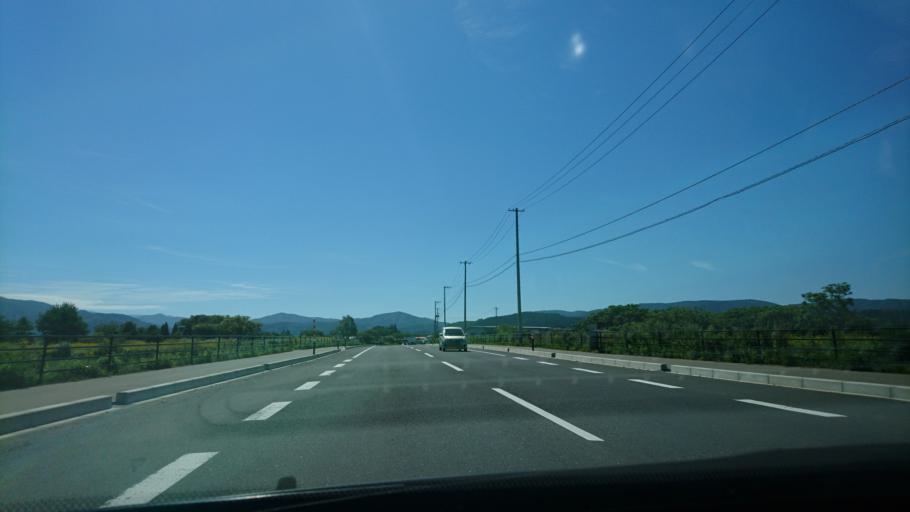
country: JP
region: Iwate
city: Tono
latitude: 39.3001
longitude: 141.5776
